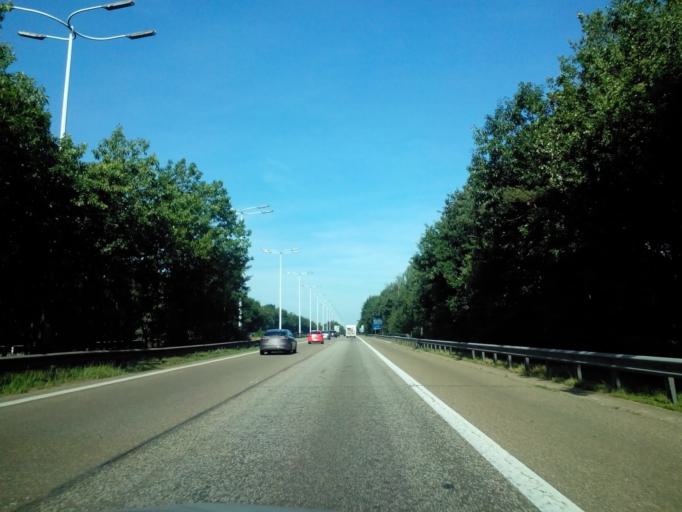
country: BE
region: Flanders
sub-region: Provincie Limburg
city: Genk
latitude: 50.9974
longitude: 5.4841
